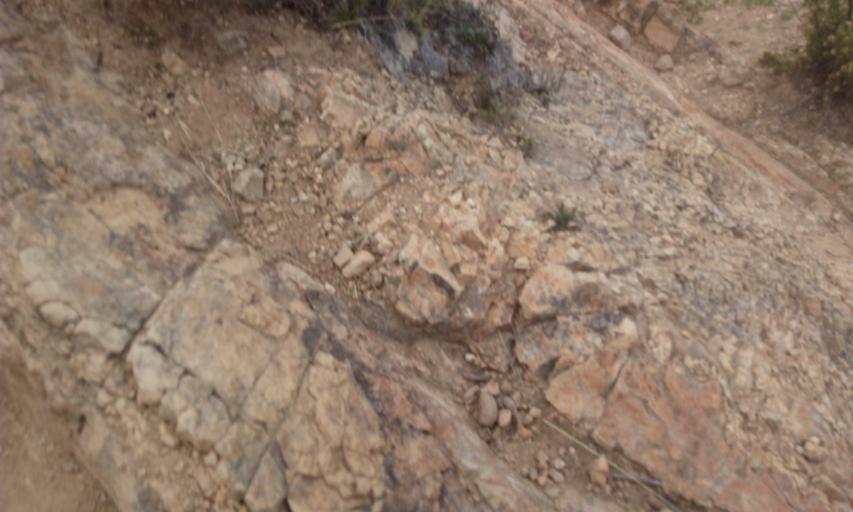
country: BO
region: La Paz
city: Yumani
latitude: -16.0476
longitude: -69.1449
